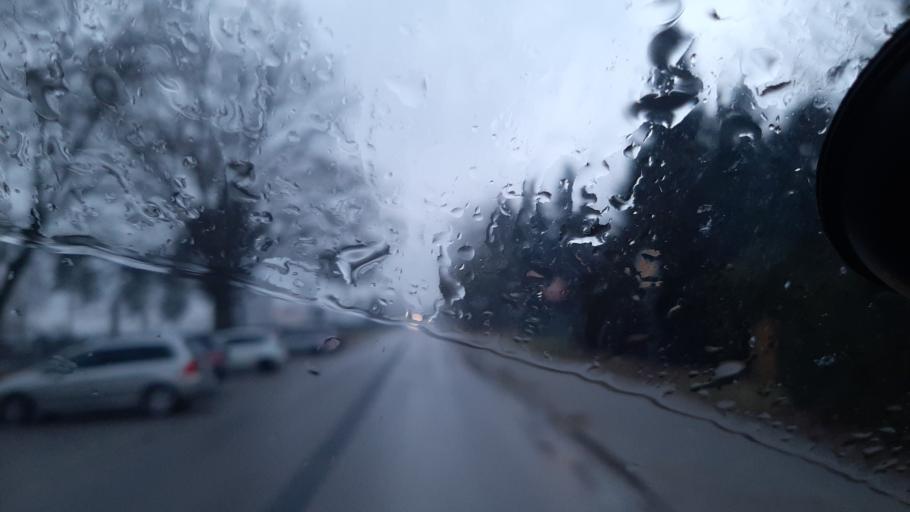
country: PL
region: Lublin Voivodeship
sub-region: Powiat lubartowski
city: Firlej
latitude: 51.5587
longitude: 22.5211
